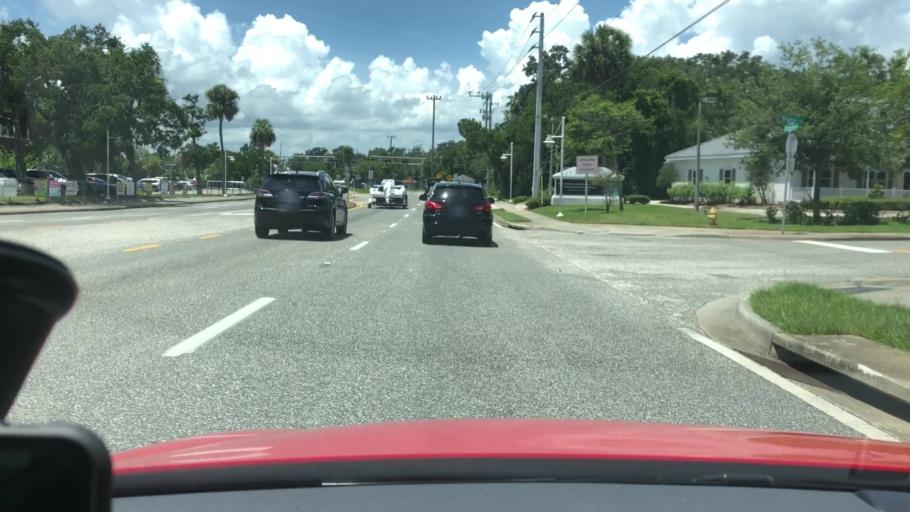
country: US
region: Florida
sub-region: Volusia County
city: South Daytona
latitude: 29.1580
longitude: -81.0139
